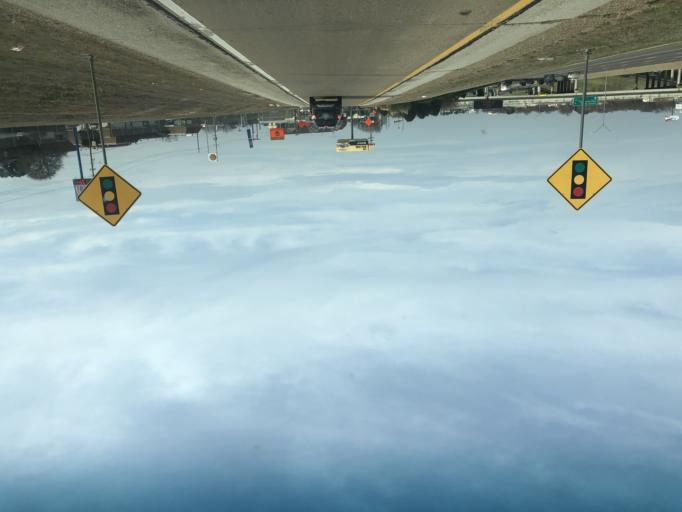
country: US
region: Texas
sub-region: Dallas County
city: Duncanville
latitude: 32.6652
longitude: -96.9108
